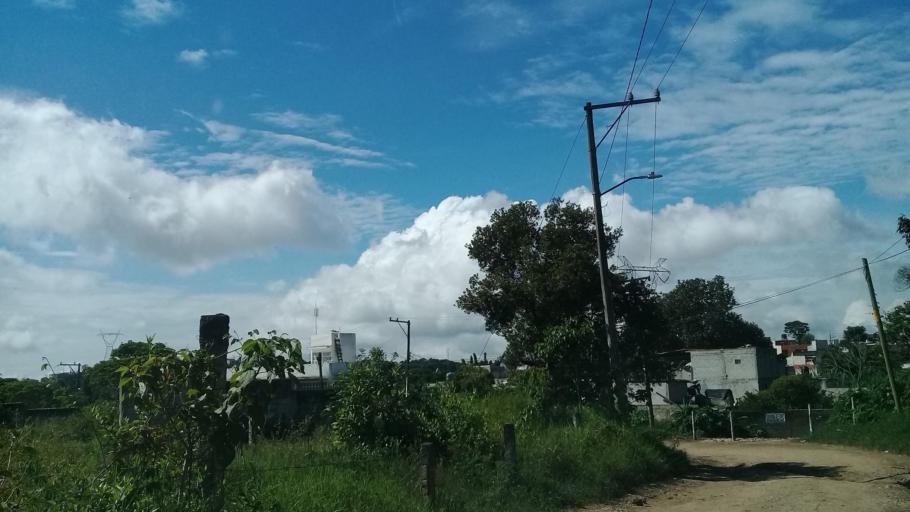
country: MX
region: Veracruz
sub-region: Jilotepec
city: El Pueblito (Garbanzal)
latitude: 19.5746
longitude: -96.9004
